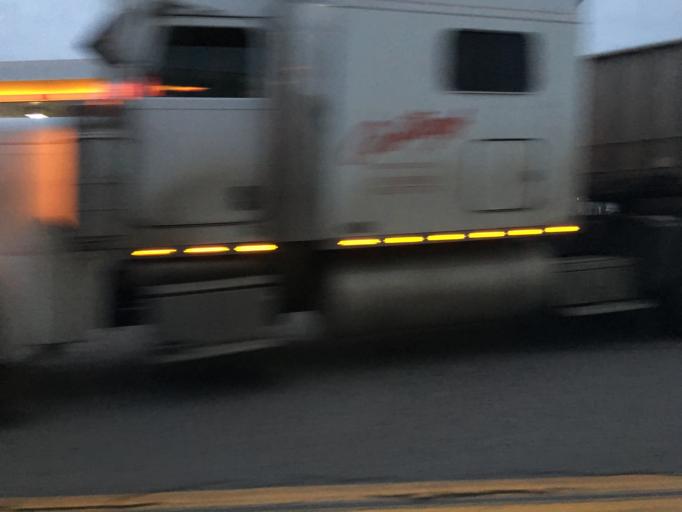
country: US
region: Colorado
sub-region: Montrose County
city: Montrose
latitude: 38.4861
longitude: -107.8676
